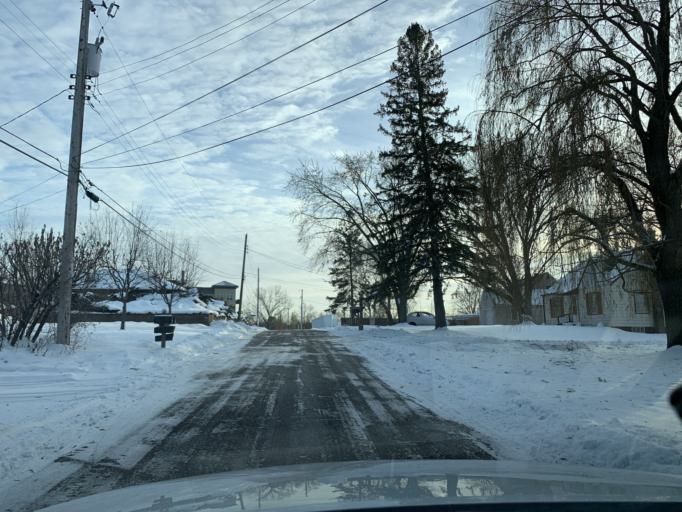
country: US
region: Minnesota
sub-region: Hennepin County
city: Minnetonka Mills
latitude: 44.9466
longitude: -93.4030
